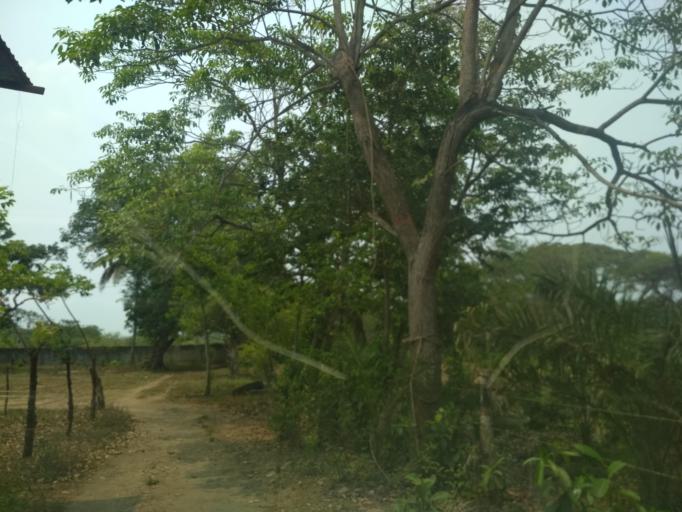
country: MX
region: Veracruz
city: El Tejar
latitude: 19.0707
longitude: -96.1540
